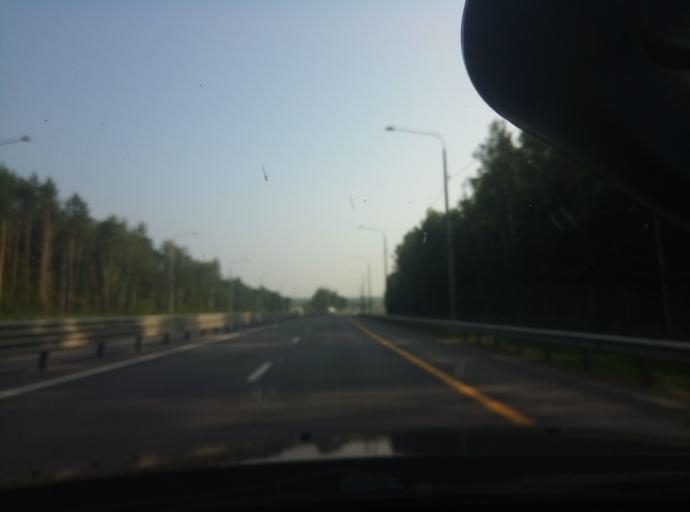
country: RU
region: Kaluga
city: Detchino
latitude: 54.8937
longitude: 36.3612
